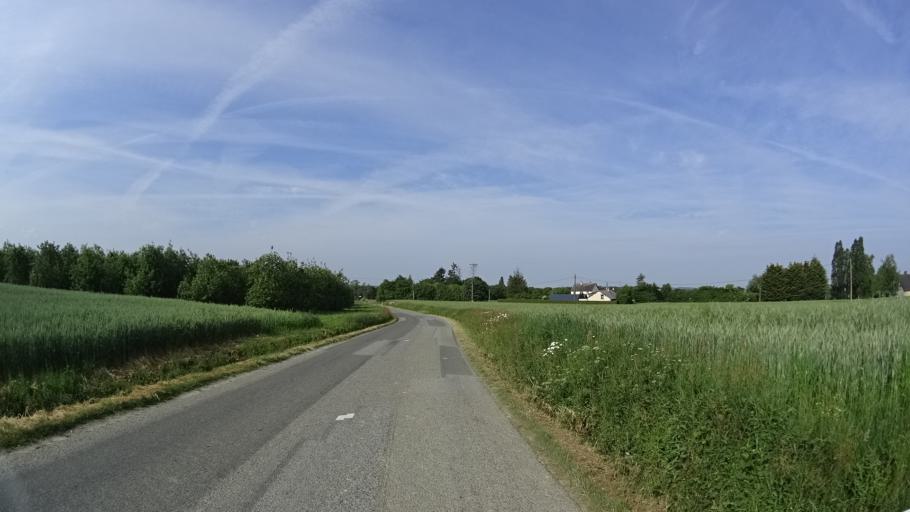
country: FR
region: Brittany
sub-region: Departement d'Ille-et-Vilaine
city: Corps-Nuds
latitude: 47.9901
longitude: -1.5721
